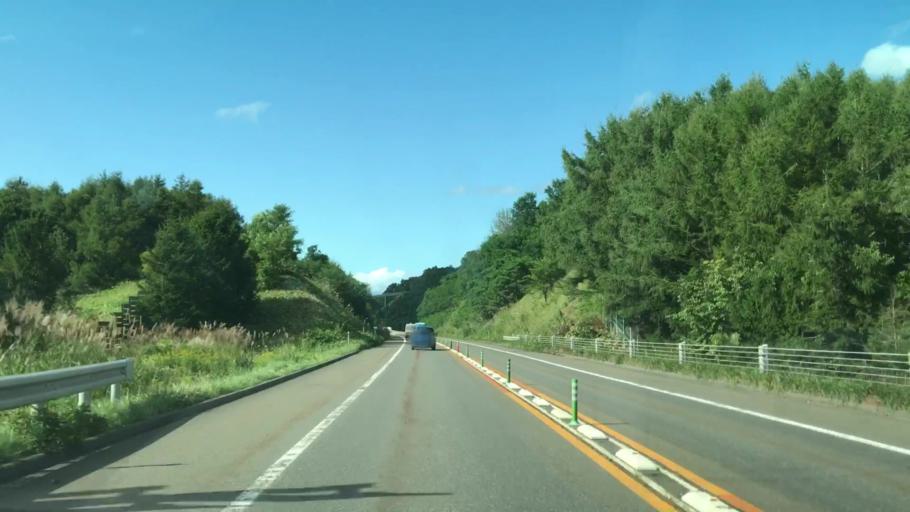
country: JP
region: Hokkaido
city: Date
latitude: 42.4548
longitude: 140.9128
